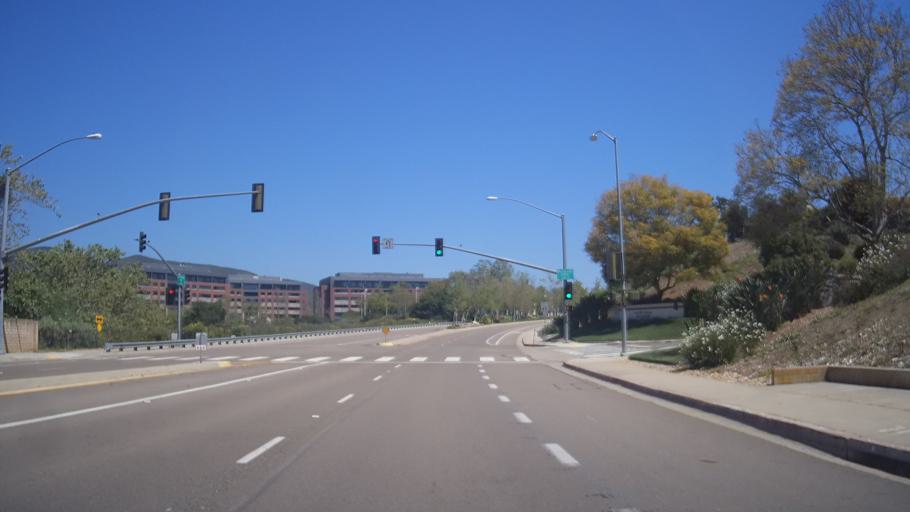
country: US
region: California
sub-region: San Diego County
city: Poway
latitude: 32.9586
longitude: -117.0934
